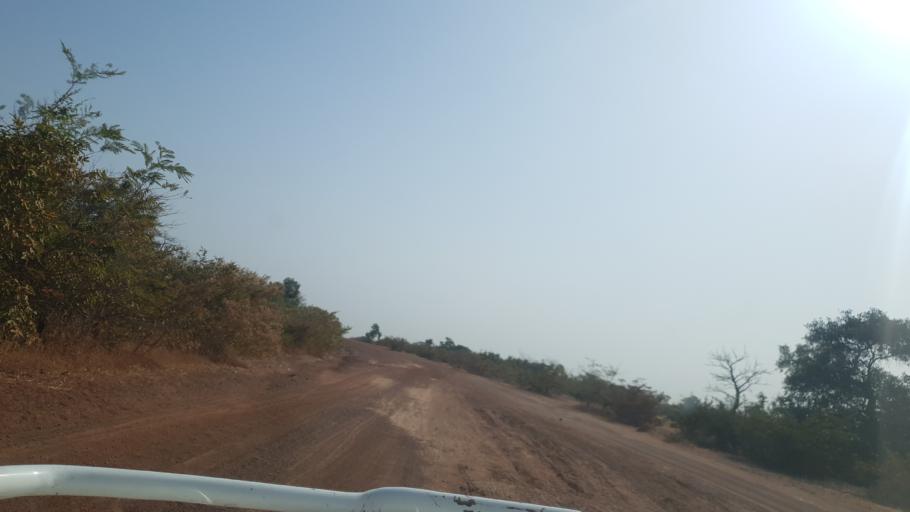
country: ML
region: Koulikoro
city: Dioila
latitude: 12.6675
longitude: -6.6989
